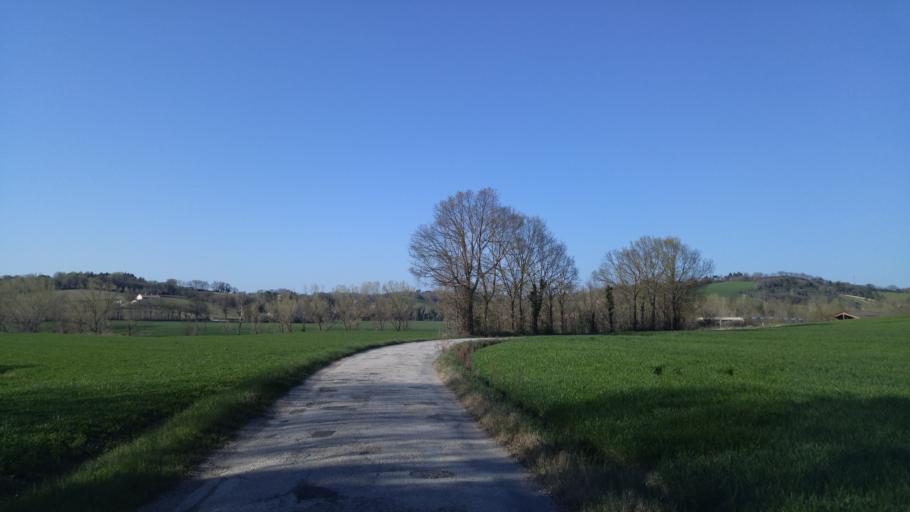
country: IT
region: The Marches
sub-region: Provincia di Pesaro e Urbino
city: Cuccurano
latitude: 43.8247
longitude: 12.9152
